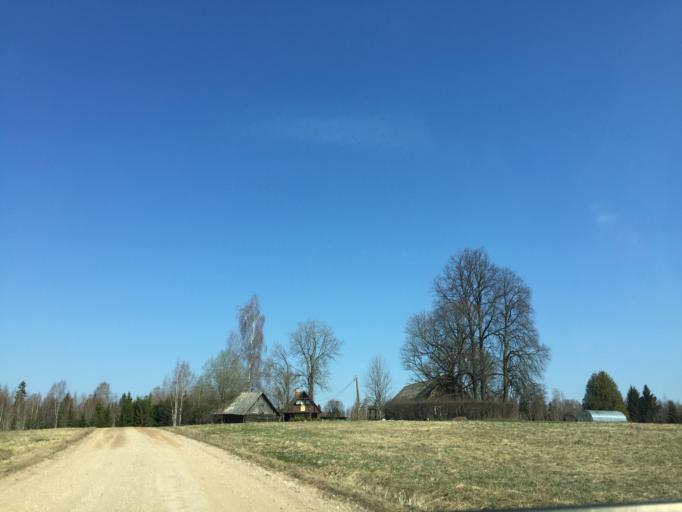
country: EE
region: Tartu
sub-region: Alatskivi vald
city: Kallaste
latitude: 58.5671
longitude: 26.9427
